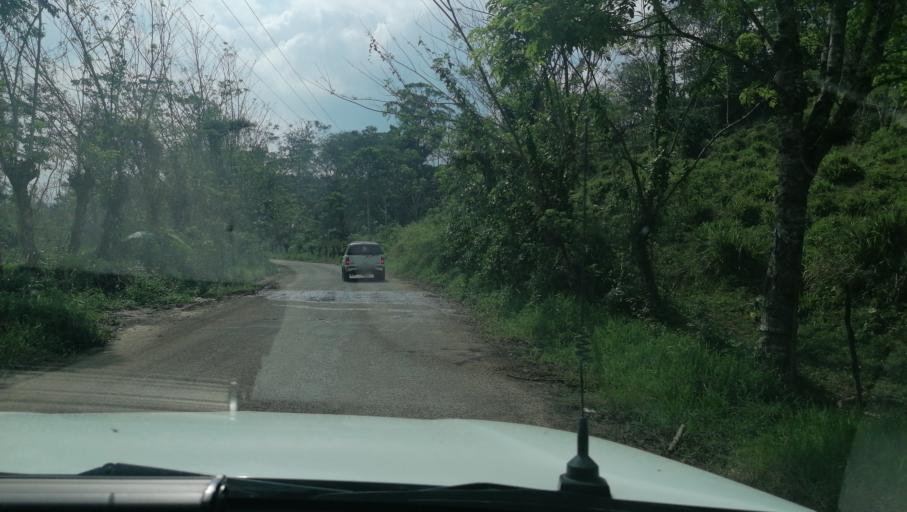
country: MX
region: Chiapas
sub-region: Francisco Leon
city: San Miguel la Sardina
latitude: 17.2341
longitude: -93.3384
